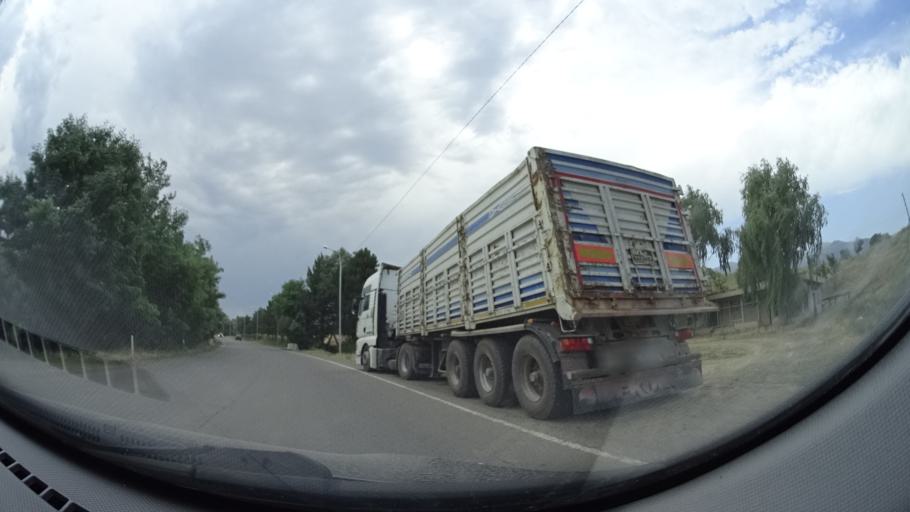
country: GE
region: Samtskhe-Javakheti
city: Aspindza
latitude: 41.5873
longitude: 43.2379
